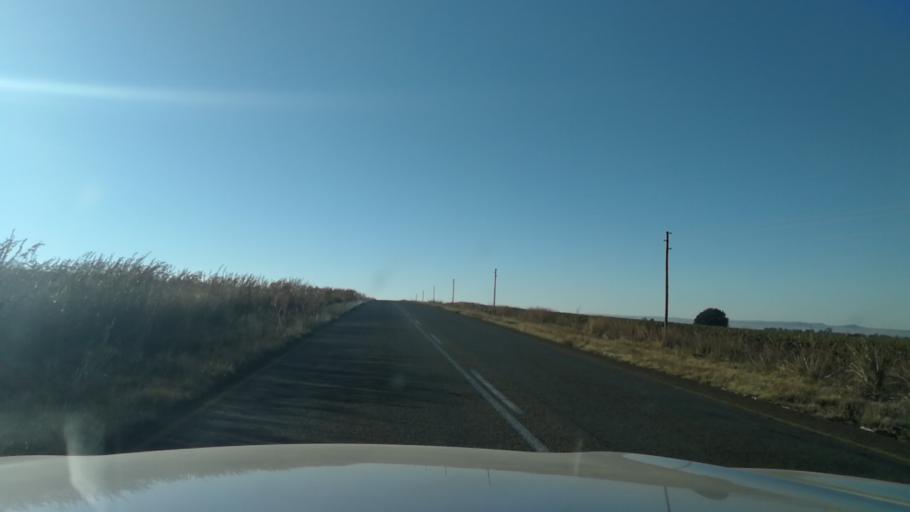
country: ZA
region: North-West
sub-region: Bojanala Platinum District Municipality
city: Koster
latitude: -25.9159
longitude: 27.0693
